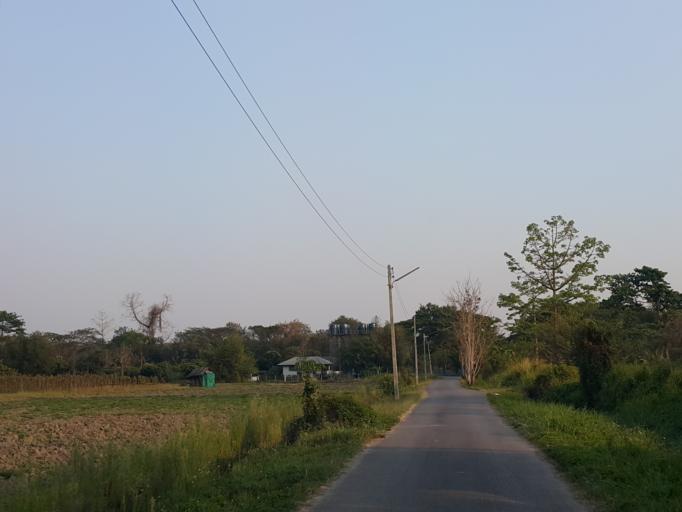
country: TH
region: Chiang Mai
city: San Sai
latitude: 18.8976
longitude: 98.9455
